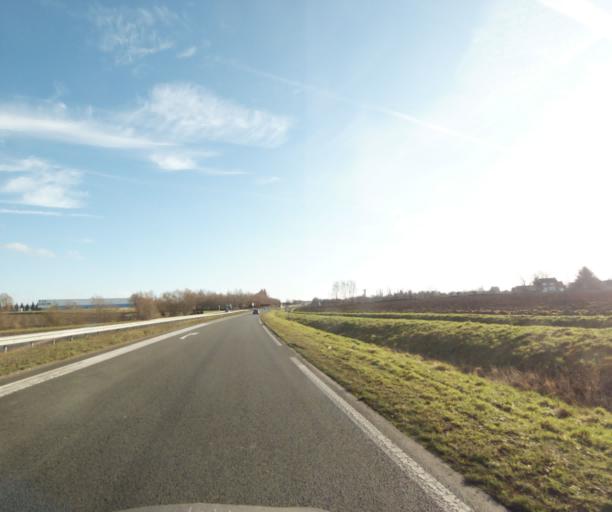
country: FR
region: Nord-Pas-de-Calais
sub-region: Departement du Nord
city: Saultain
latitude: 50.3435
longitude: 3.5816
